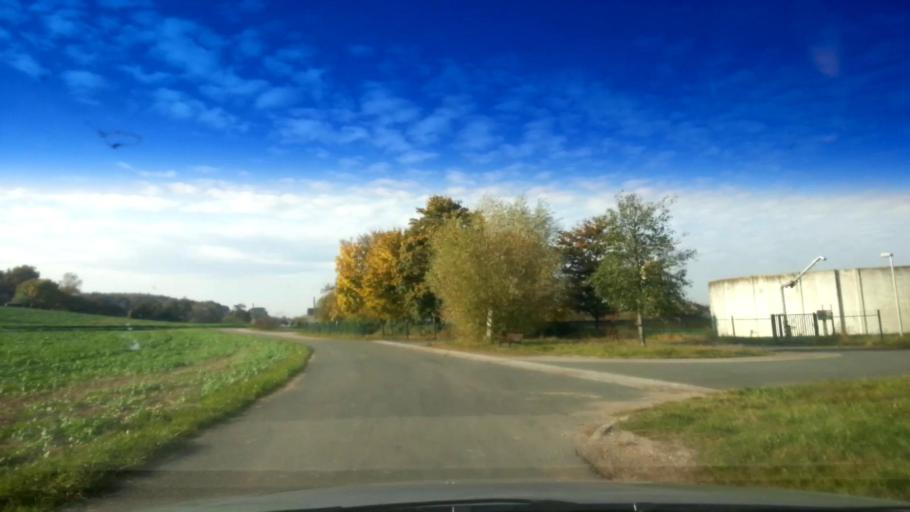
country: DE
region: Bavaria
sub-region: Upper Franconia
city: Stegaurach
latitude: 49.8510
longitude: 10.8683
